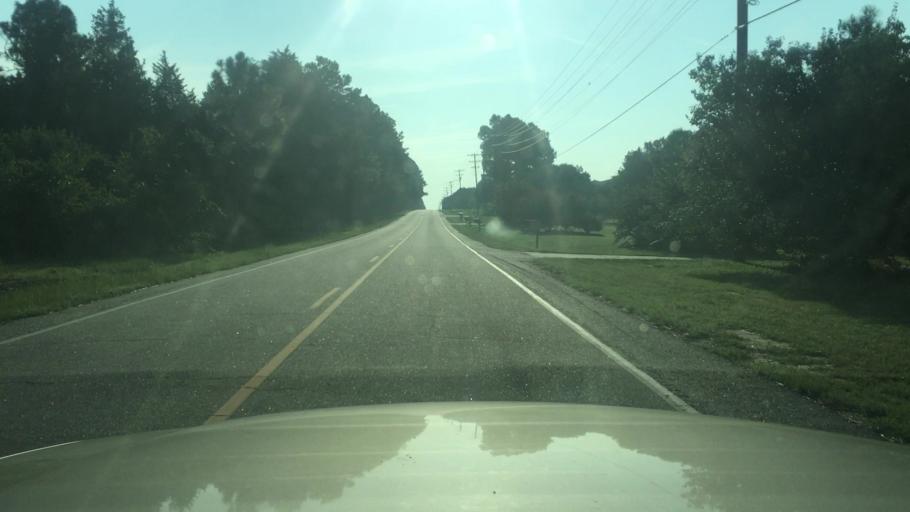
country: US
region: North Carolina
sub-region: Harnett County
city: Walkertown
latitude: 35.2071
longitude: -78.8754
